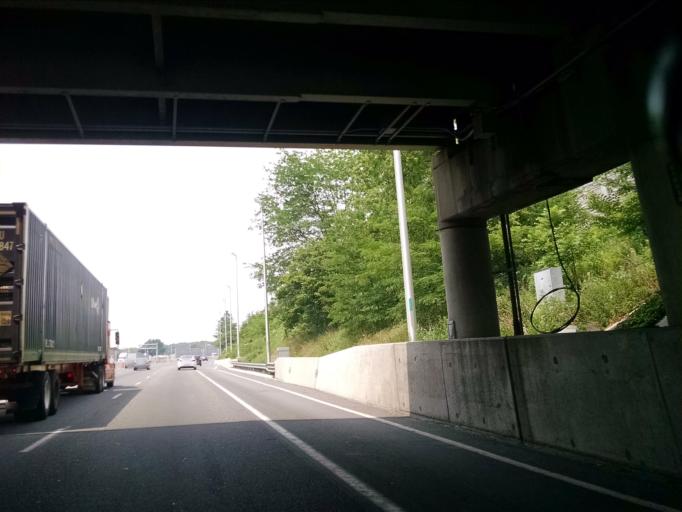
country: US
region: New York
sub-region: Richmond County
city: Bloomfield
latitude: 40.6078
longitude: -74.1408
